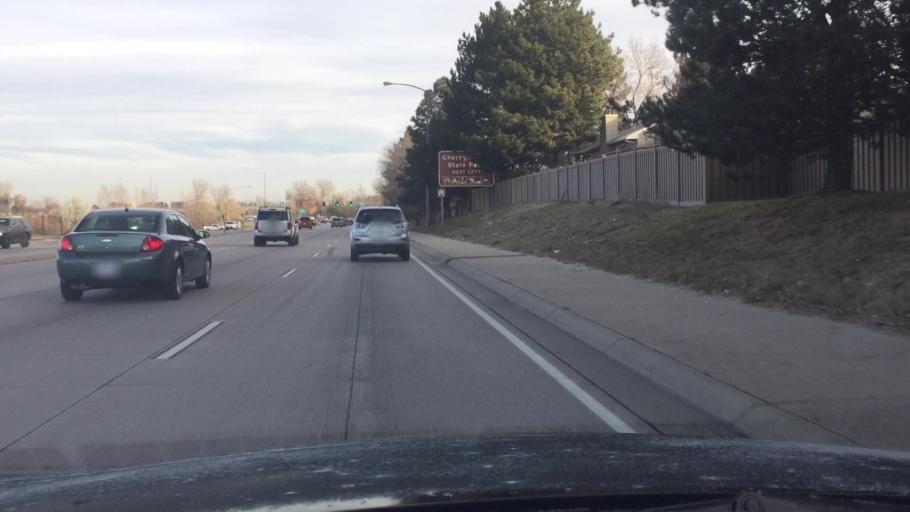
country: US
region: Colorado
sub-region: Arapahoe County
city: Dove Valley
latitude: 39.6452
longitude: -104.8287
